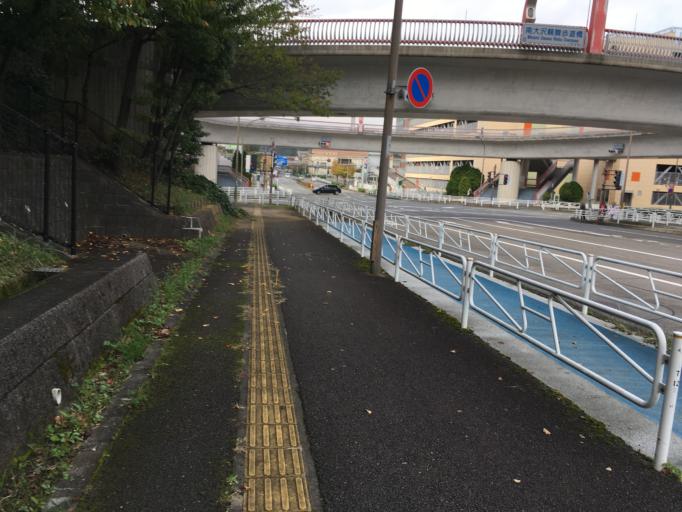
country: JP
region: Tokyo
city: Hino
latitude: 35.6116
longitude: 139.3787
